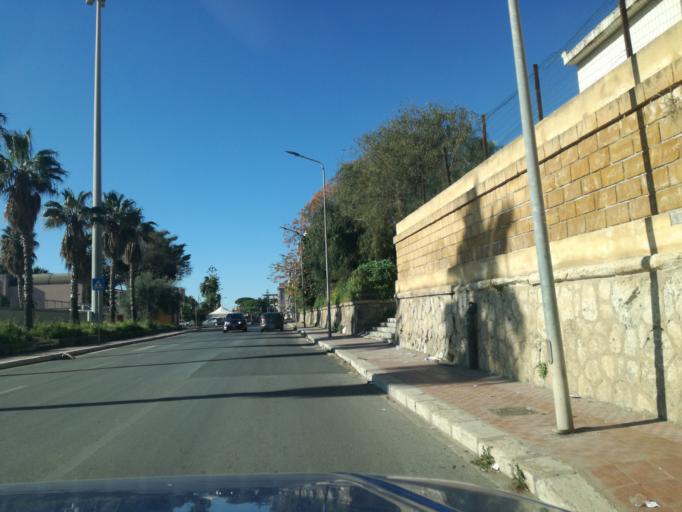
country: IT
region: Sicily
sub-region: Provincia di Caltanissetta
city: Gela
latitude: 37.0720
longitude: 14.2300
